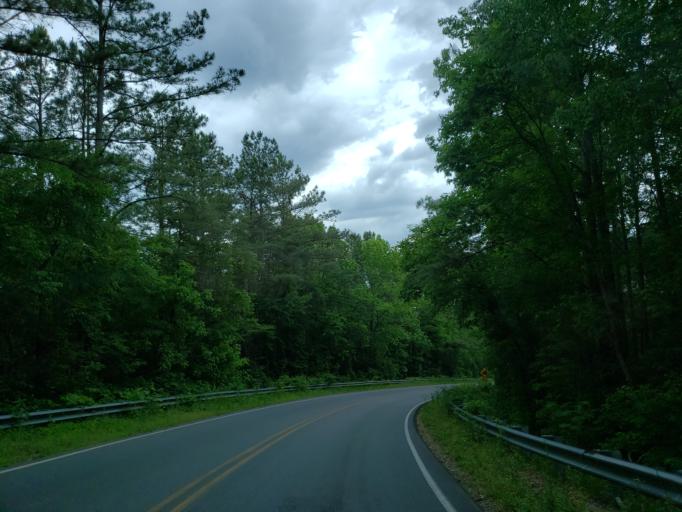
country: US
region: Georgia
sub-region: Polk County
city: Rockmart
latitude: 33.9625
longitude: -85.0507
